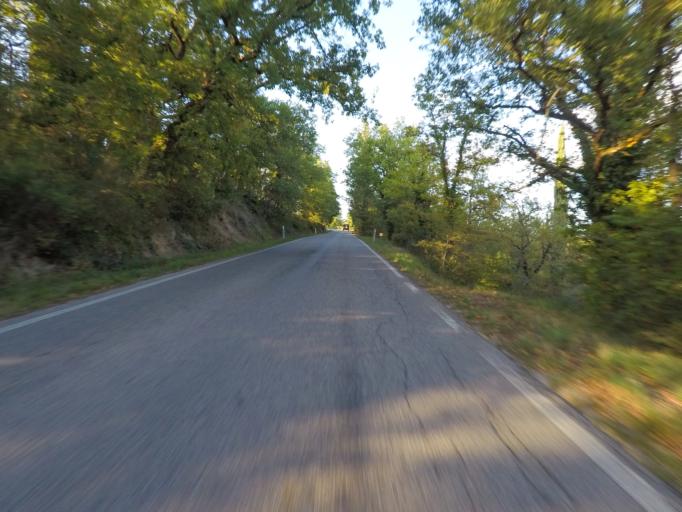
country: IT
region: Tuscany
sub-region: Provincia di Siena
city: Radda in Chianti
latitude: 43.4753
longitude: 11.3739
